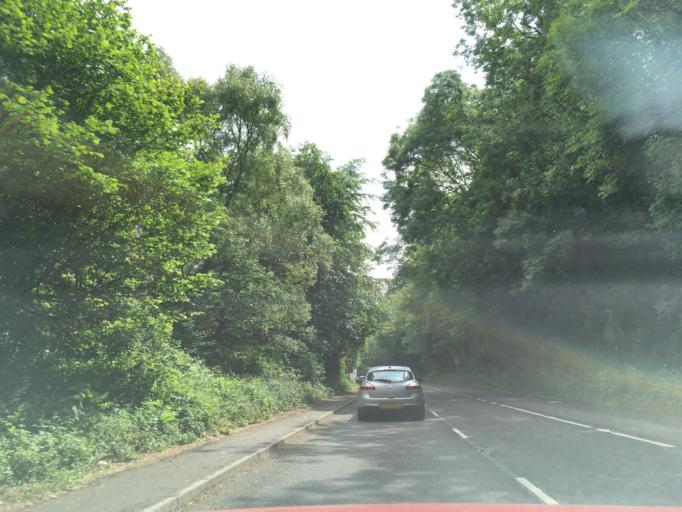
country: GB
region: England
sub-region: Devon
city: Totnes
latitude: 50.4290
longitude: -3.6919
